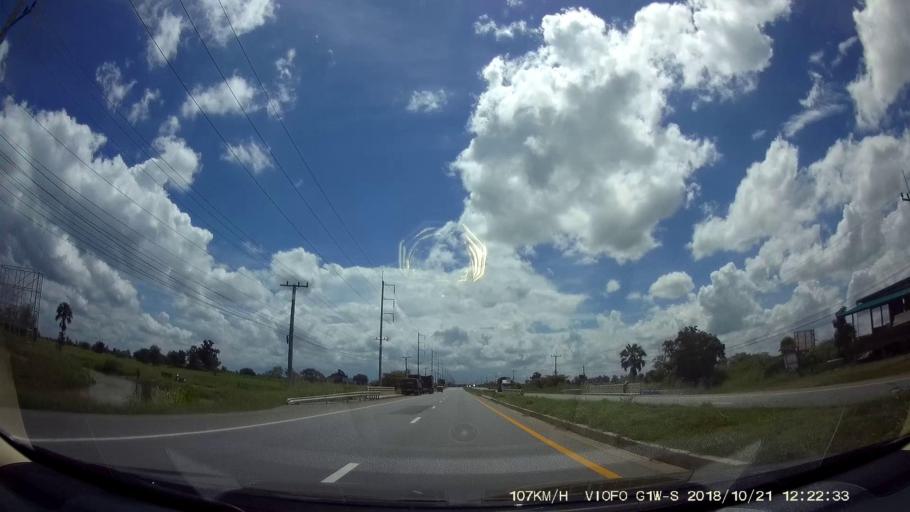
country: TH
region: Nakhon Ratchasima
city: Dan Khun Thot
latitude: 15.2595
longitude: 101.7895
